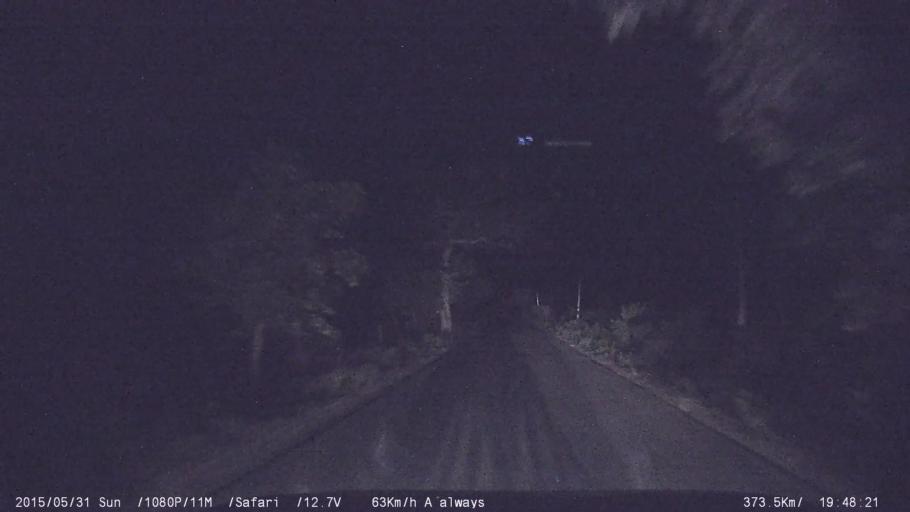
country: IN
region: Karnataka
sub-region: Mandya
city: Malavalli
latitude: 12.3083
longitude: 77.0725
